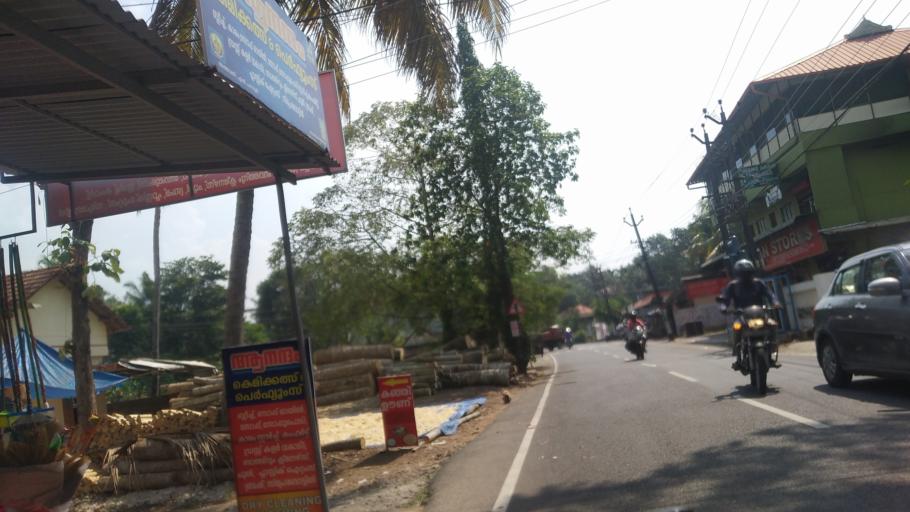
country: IN
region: Kerala
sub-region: Ernakulam
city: Elur
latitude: 10.1315
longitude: 76.2332
